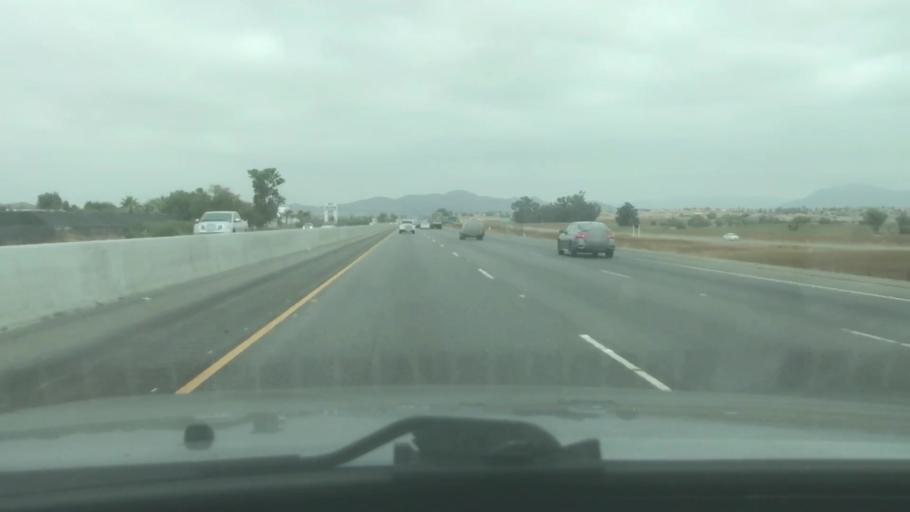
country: US
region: California
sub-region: Riverside County
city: Sun City
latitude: 33.6474
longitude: -117.1713
